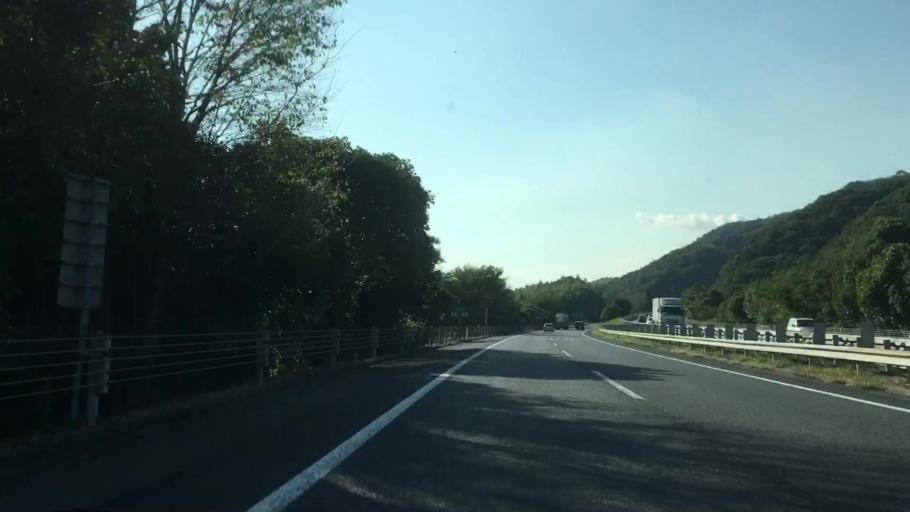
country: JP
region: Yamaguchi
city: Kudamatsu
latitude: 34.0418
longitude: 131.9004
